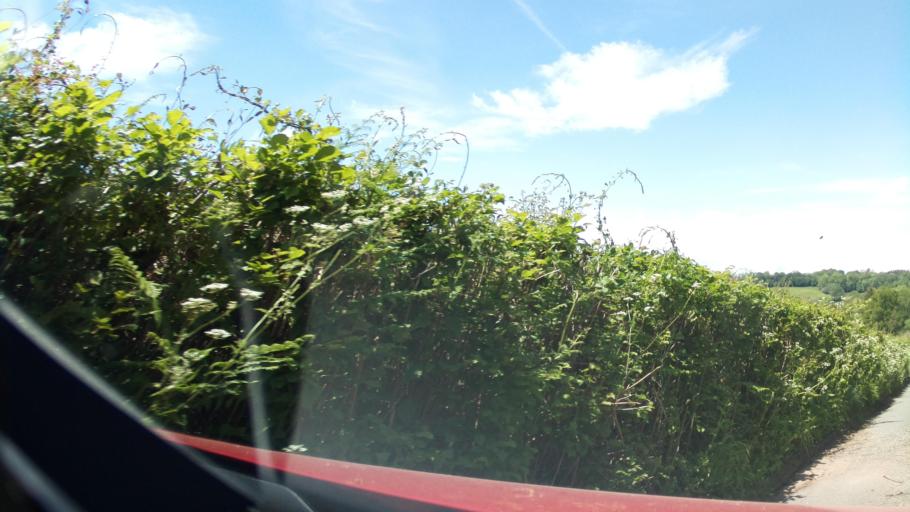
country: GB
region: Wales
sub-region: Monmouthshire
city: Tintern
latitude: 51.6653
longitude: -2.7507
